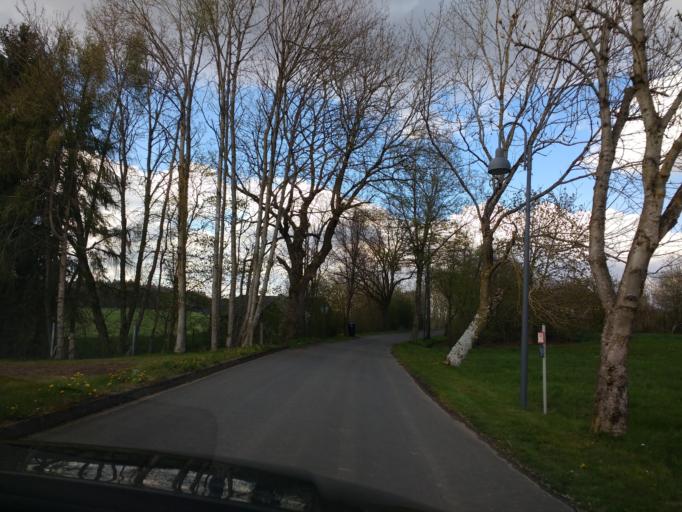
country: DE
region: Rheinland-Pfalz
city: Oberehe-Stroheich
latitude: 50.2884
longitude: 6.7539
